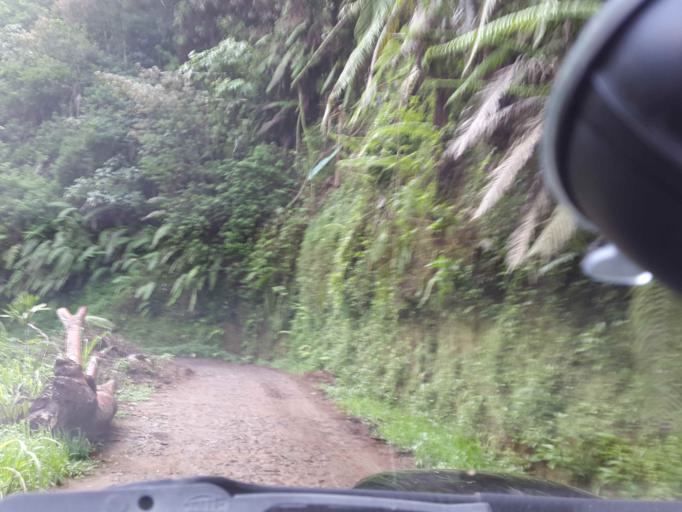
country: ID
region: Central Java
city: Wonosobo
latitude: -7.4058
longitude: 110.0339
